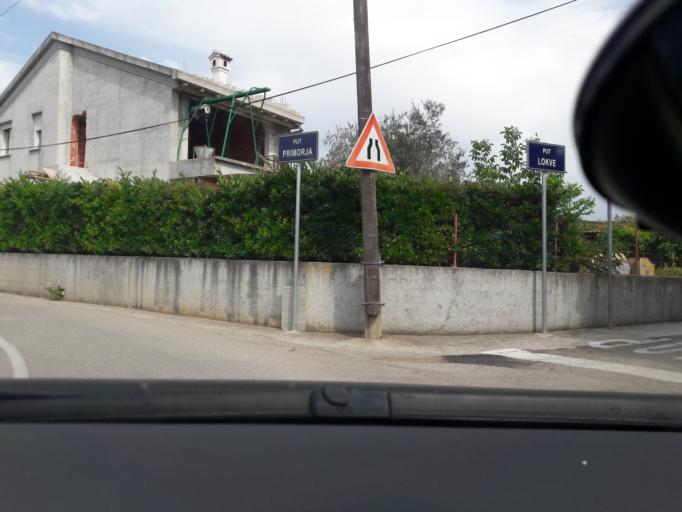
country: HR
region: Zadarska
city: Nin
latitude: 44.1693
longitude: 15.1916
